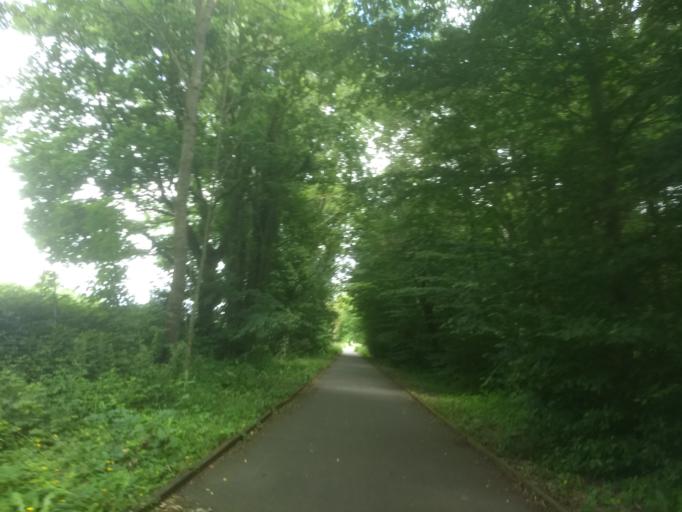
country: FR
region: Nord-Pas-de-Calais
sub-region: Departement du Pas-de-Calais
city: Beaumetz-les-Loges
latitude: 50.2375
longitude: 2.6568
